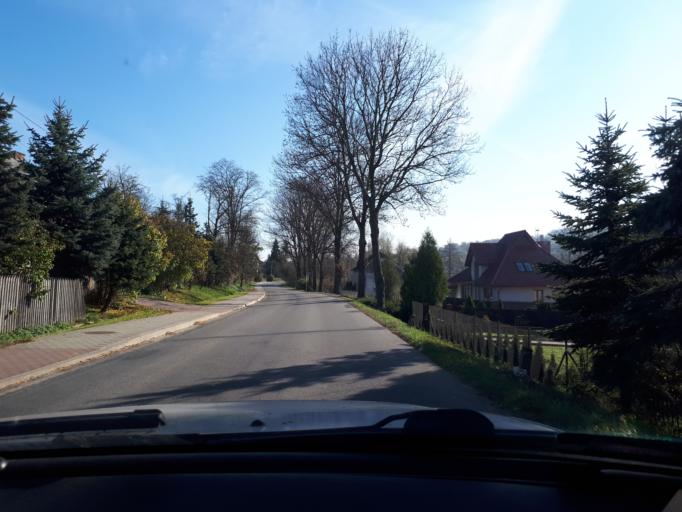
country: PL
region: Subcarpathian Voivodeship
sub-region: Powiat debicki
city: Debica
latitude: 49.9994
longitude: 21.4145
